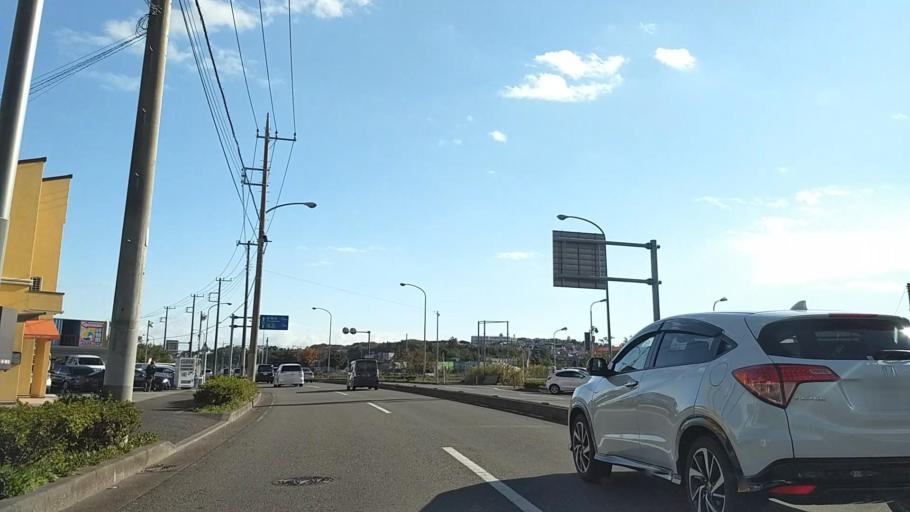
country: JP
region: Tokyo
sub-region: Machida-shi
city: Machida
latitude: 35.5646
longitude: 139.5145
